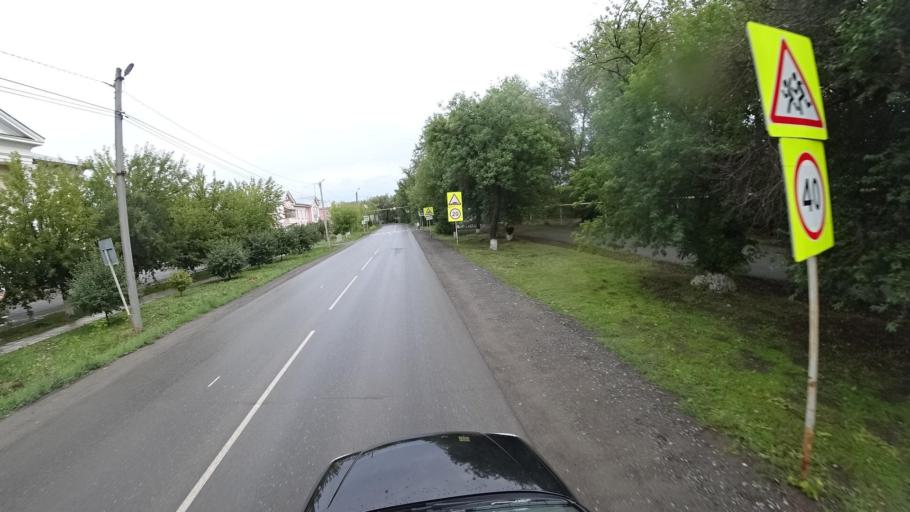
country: RU
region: Sverdlovsk
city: Kamyshlov
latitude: 56.8513
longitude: 62.7106
